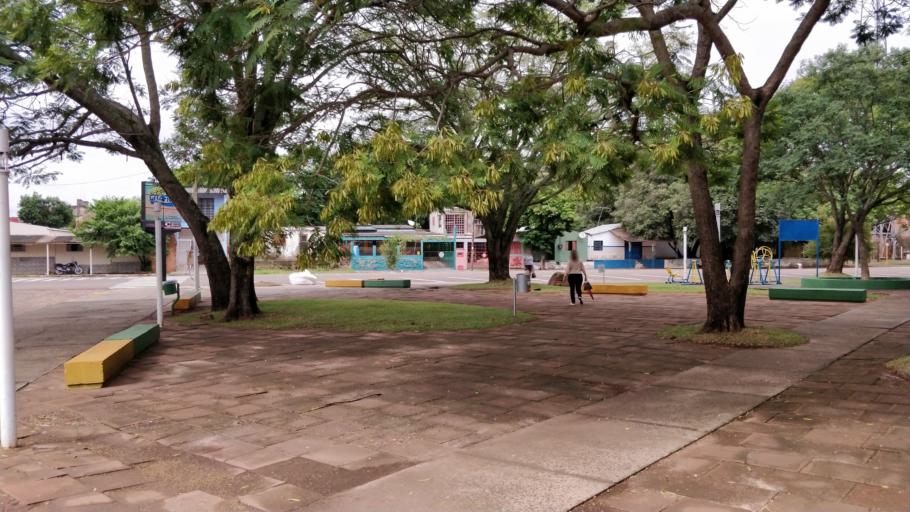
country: BR
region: Rio Grande do Sul
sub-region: Itaqui
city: Itaqui
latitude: -29.1185
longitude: -56.5549
